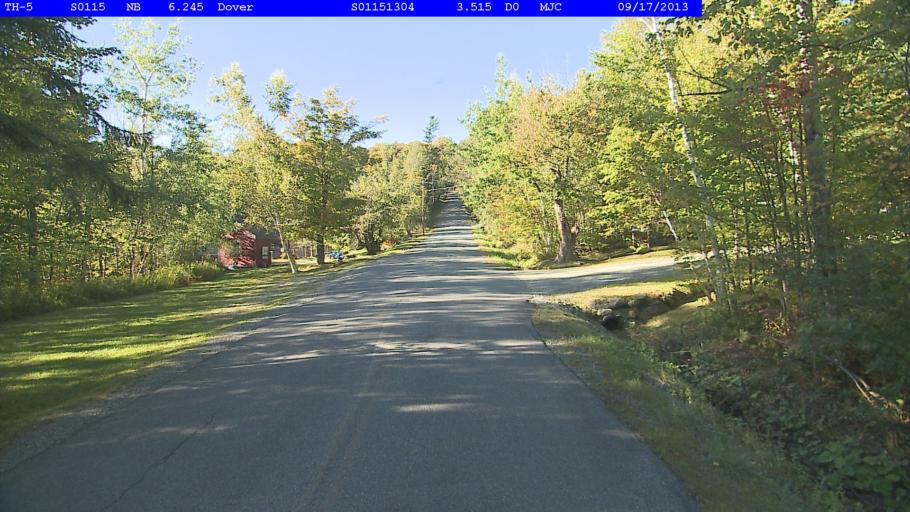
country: US
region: Vermont
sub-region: Windham County
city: Dover
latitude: 42.9740
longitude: -72.8921
